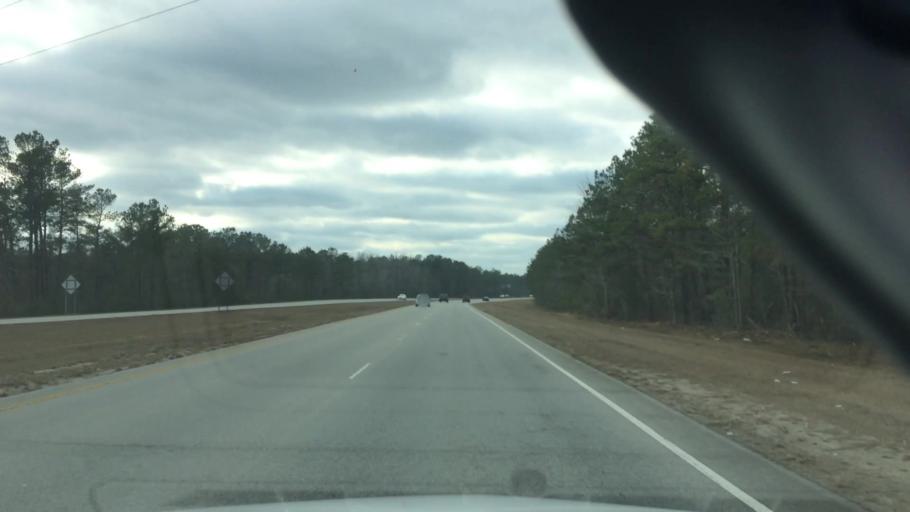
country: US
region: North Carolina
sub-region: Brunswick County
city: Bolivia
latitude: 34.0792
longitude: -78.1421
